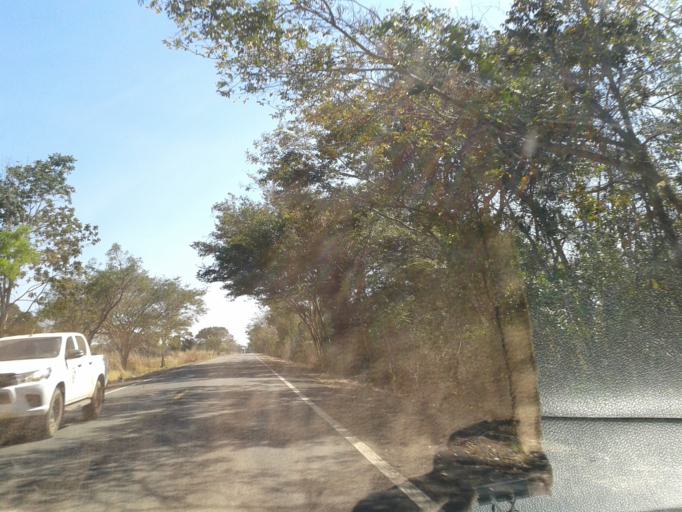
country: BR
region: Goias
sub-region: Sao Miguel Do Araguaia
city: Sao Miguel do Araguaia
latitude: -13.9231
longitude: -50.3223
